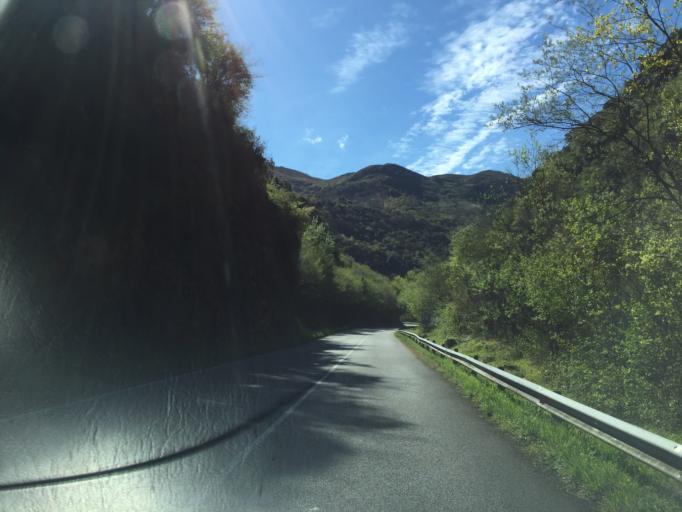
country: ES
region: Asturias
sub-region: Province of Asturias
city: Proaza
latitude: 43.2971
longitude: -5.9852
